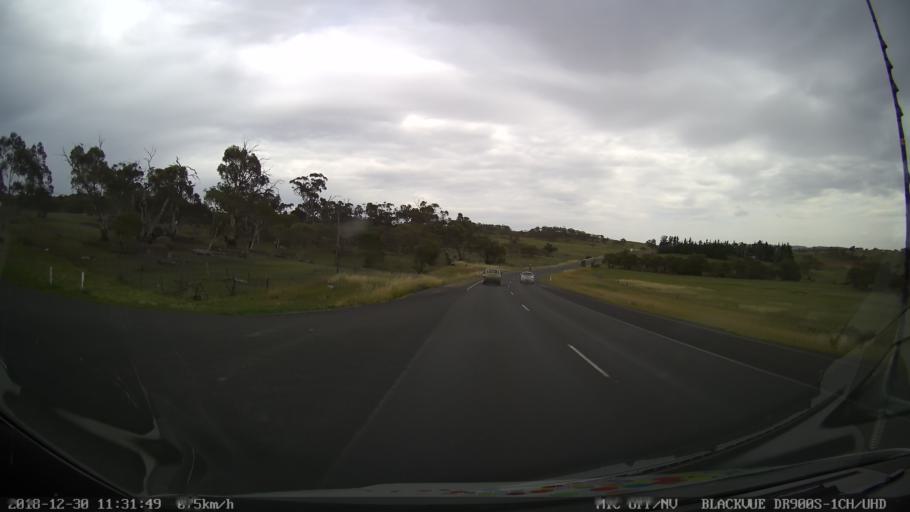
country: AU
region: New South Wales
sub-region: Snowy River
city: Jindabyne
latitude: -36.4278
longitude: 148.6093
